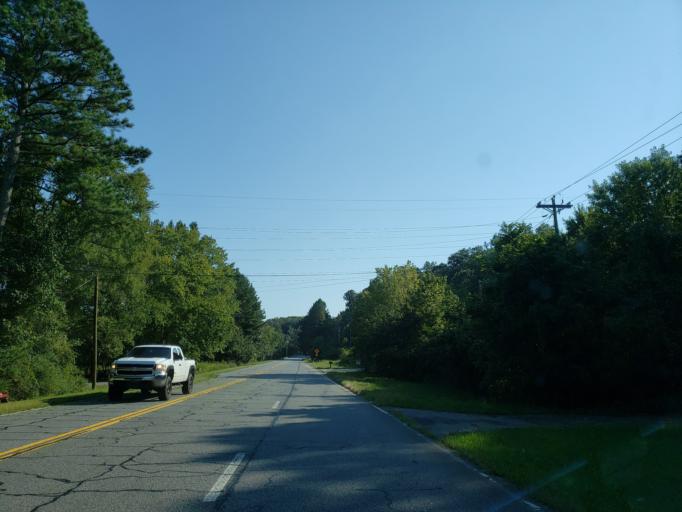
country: US
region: Georgia
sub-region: Whitfield County
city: Varnell
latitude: 34.8828
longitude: -84.9778
